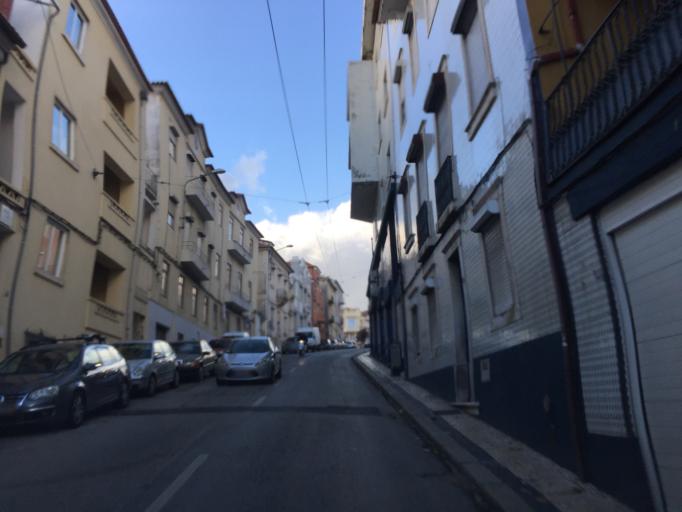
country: PT
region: Coimbra
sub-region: Coimbra
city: Coimbra
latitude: 40.2127
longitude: -8.4271
